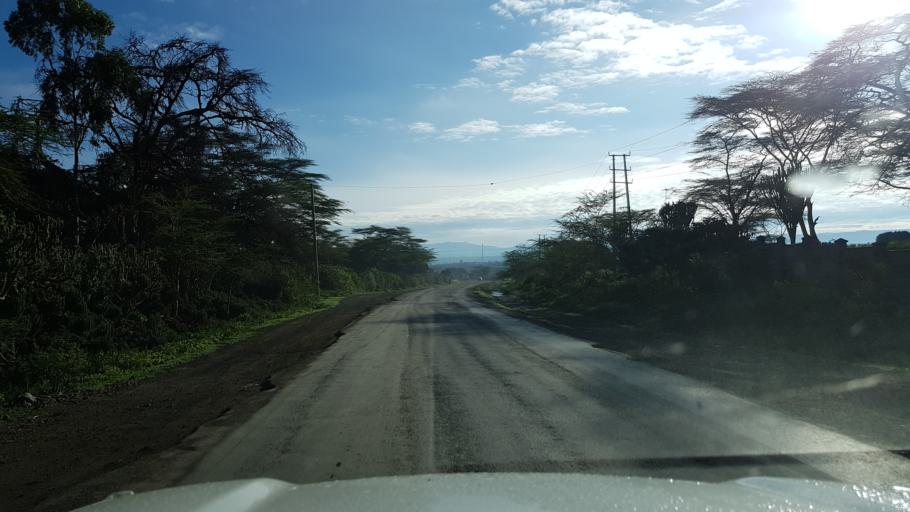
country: KE
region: Nakuru
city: Naivasha
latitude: -0.8031
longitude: 36.4142
